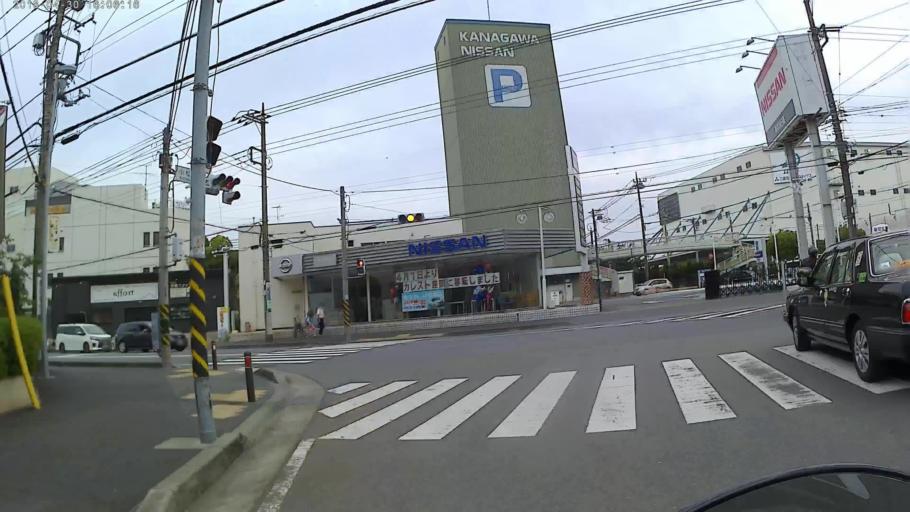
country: JP
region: Kanagawa
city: Minami-rinkan
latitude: 35.5017
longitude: 139.4286
